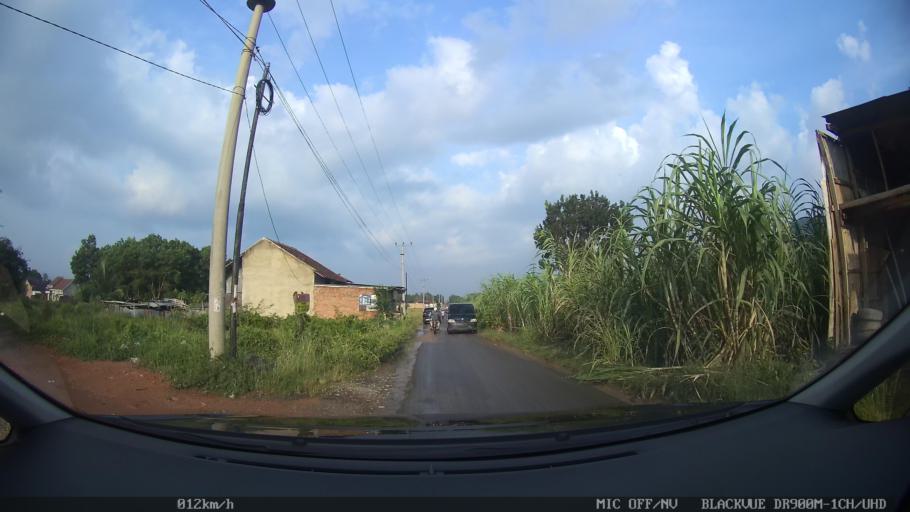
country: ID
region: Lampung
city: Kedaton
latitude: -5.3919
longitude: 105.3242
